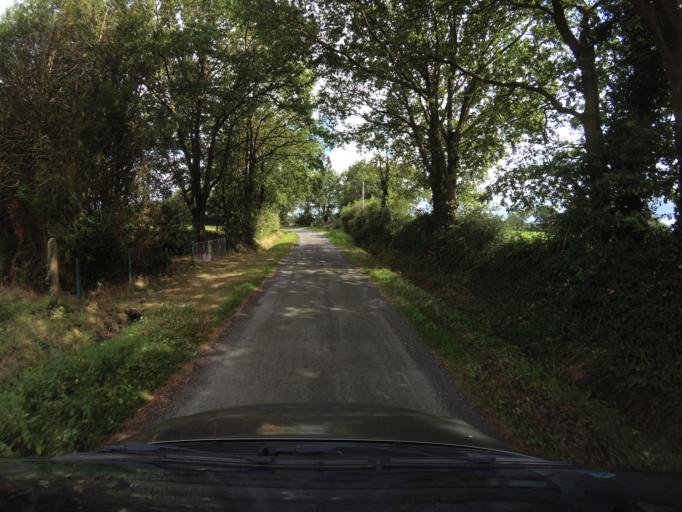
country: FR
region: Pays de la Loire
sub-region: Departement de la Vendee
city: Saint-Philbert-de-Bouaine
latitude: 46.9927
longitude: -1.4840
